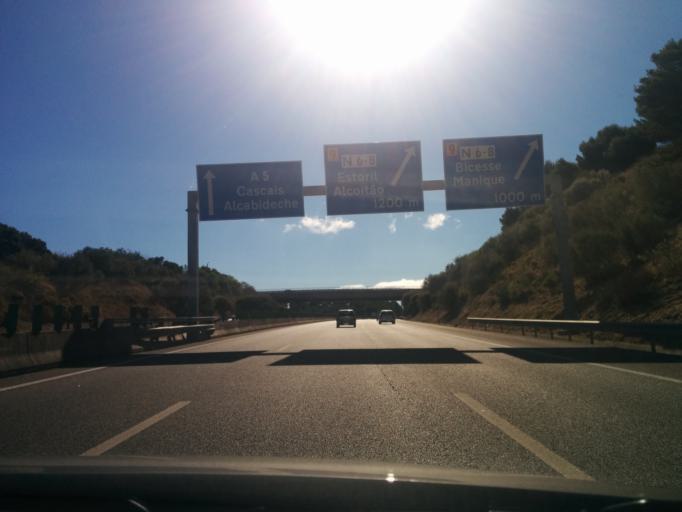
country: PT
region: Lisbon
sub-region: Cascais
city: Estoril
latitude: 38.7183
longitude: -9.3713
